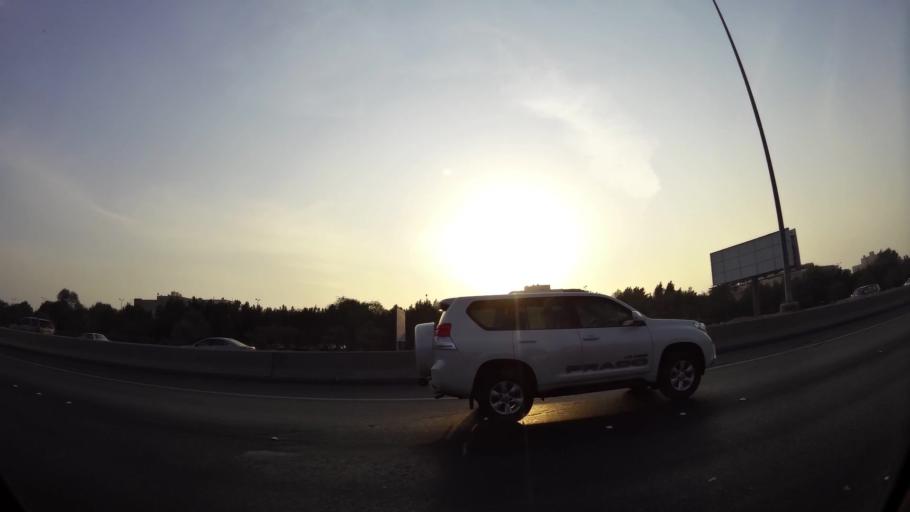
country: KW
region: Muhafazat Hawalli
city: Salwa
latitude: 29.2857
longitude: 48.0749
